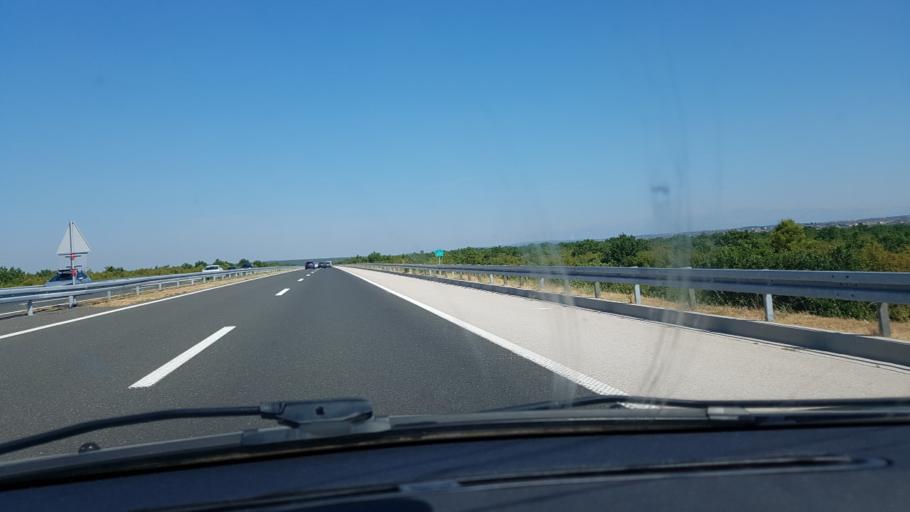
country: HR
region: Zadarska
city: Benkovac
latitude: 43.9773
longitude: 15.6406
